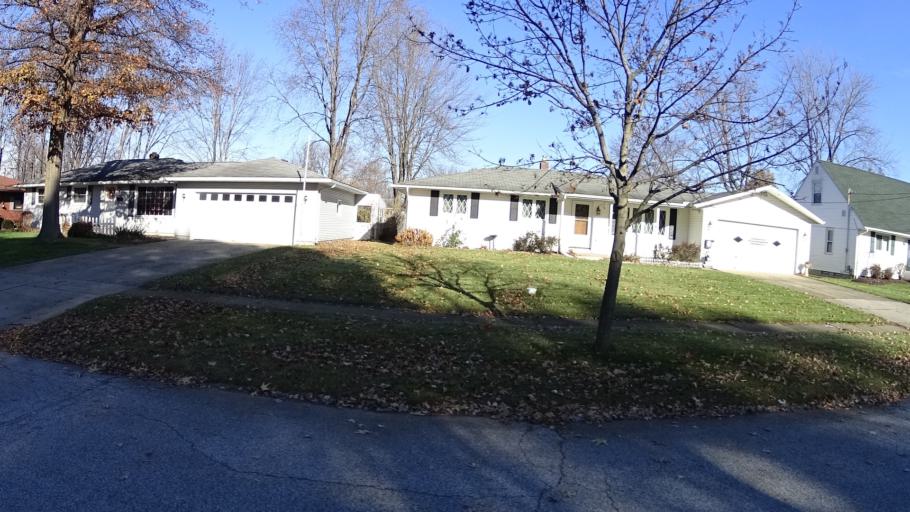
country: US
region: Ohio
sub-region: Lorain County
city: Sheffield
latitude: 41.3938
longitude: -82.0706
